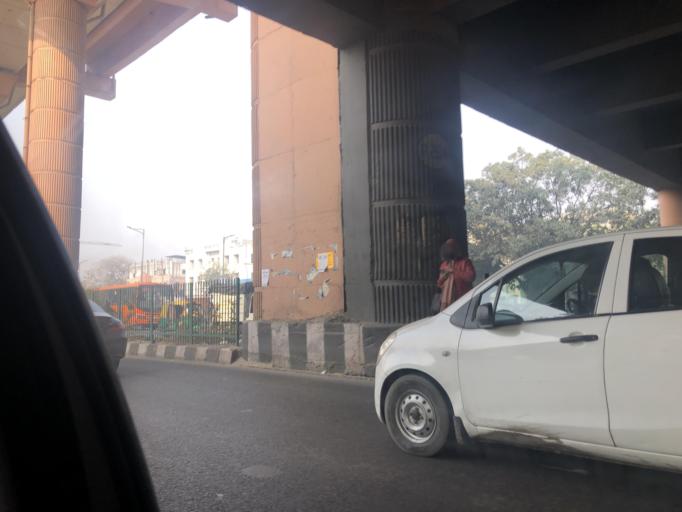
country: IN
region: NCT
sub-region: West Delhi
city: Nangloi Jat
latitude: 28.6797
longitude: 77.0926
